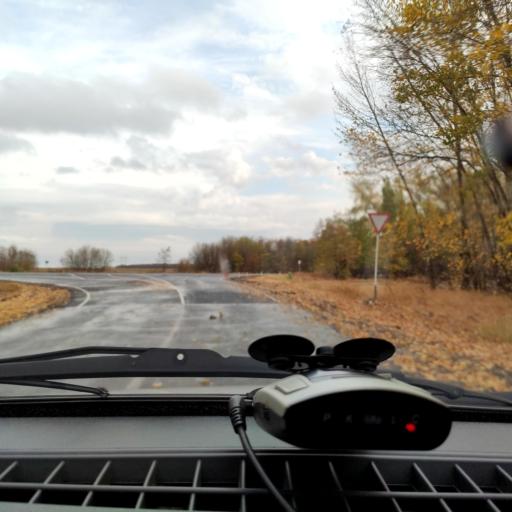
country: RU
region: Voronezj
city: Uryv-Pokrovka
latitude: 51.2301
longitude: 39.0586
